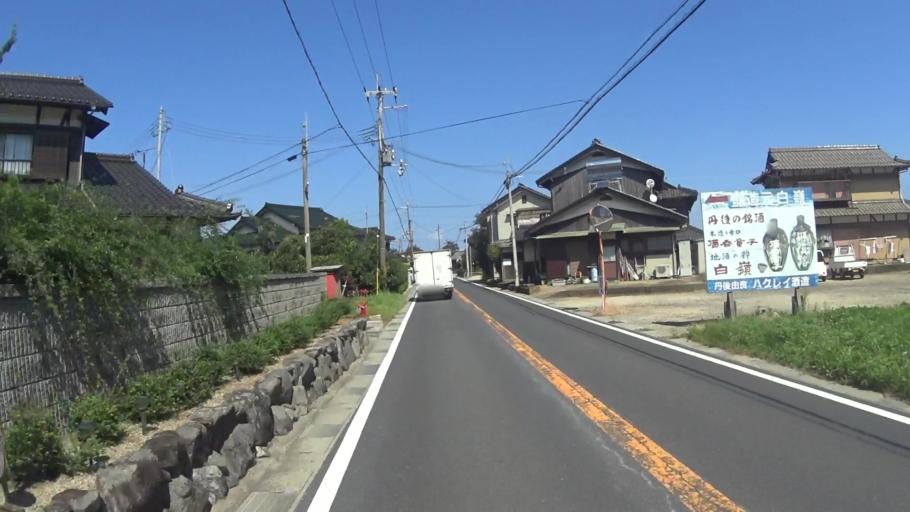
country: JP
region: Kyoto
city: Maizuru
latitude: 35.5126
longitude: 135.2848
